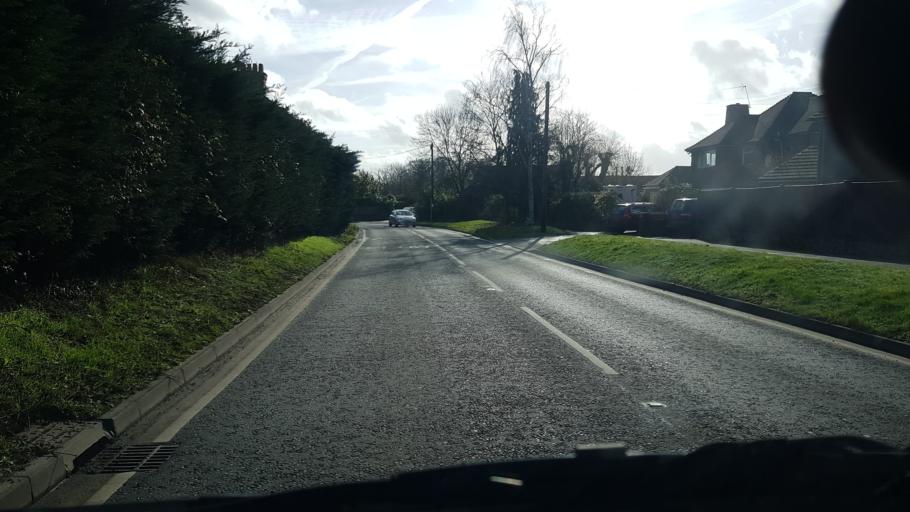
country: GB
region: England
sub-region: Surrey
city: Guildford
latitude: 51.2688
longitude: -0.5663
